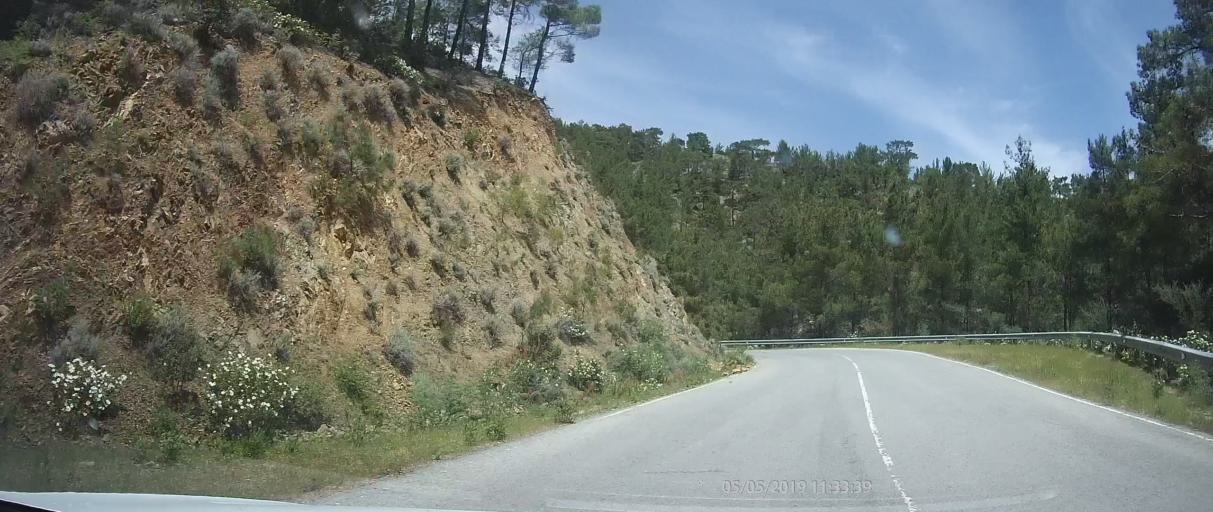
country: CY
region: Lefkosia
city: Kato Pyrgos
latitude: 34.9626
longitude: 32.6458
